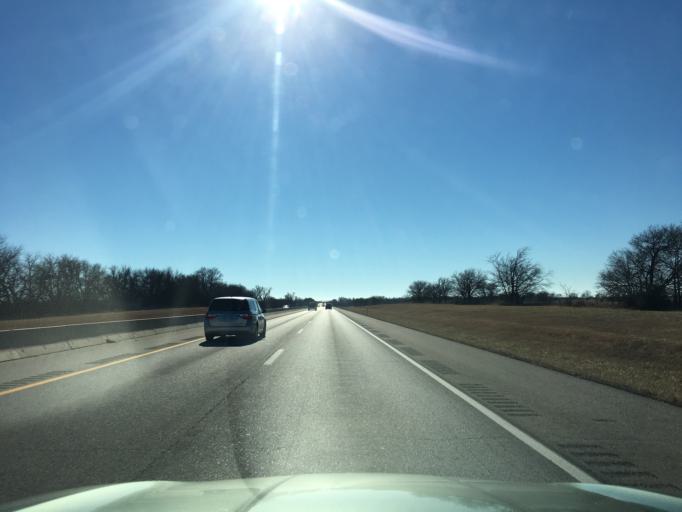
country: US
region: Kansas
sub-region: Sumner County
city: Wellington
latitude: 37.0973
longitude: -97.3387
